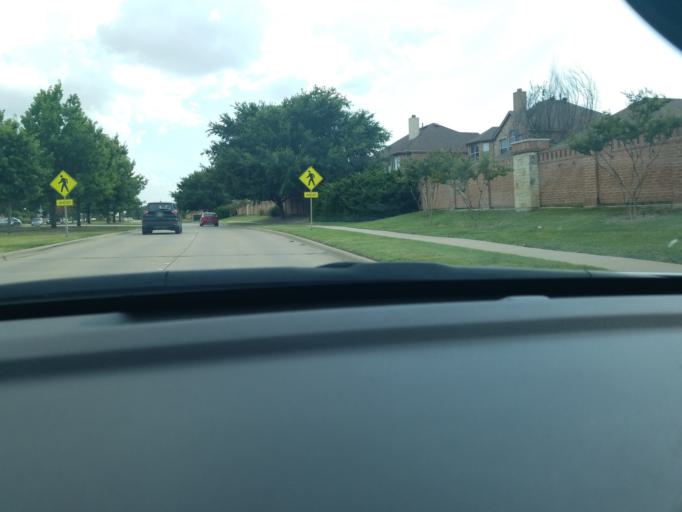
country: US
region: Texas
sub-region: Denton County
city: Little Elm
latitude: 33.1765
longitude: -96.8944
